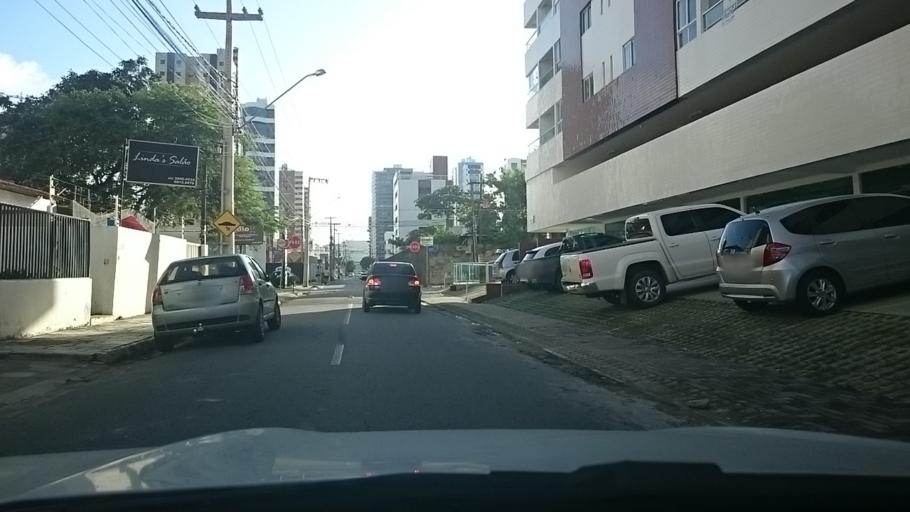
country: BR
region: Paraiba
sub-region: Joao Pessoa
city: Joao Pessoa
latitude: -7.0988
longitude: -34.8382
